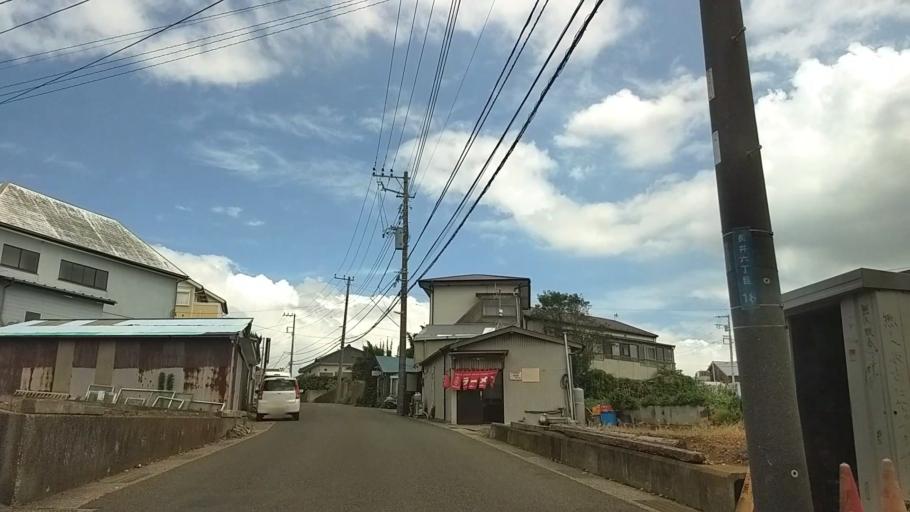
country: JP
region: Kanagawa
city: Miura
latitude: 35.1977
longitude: 139.6086
